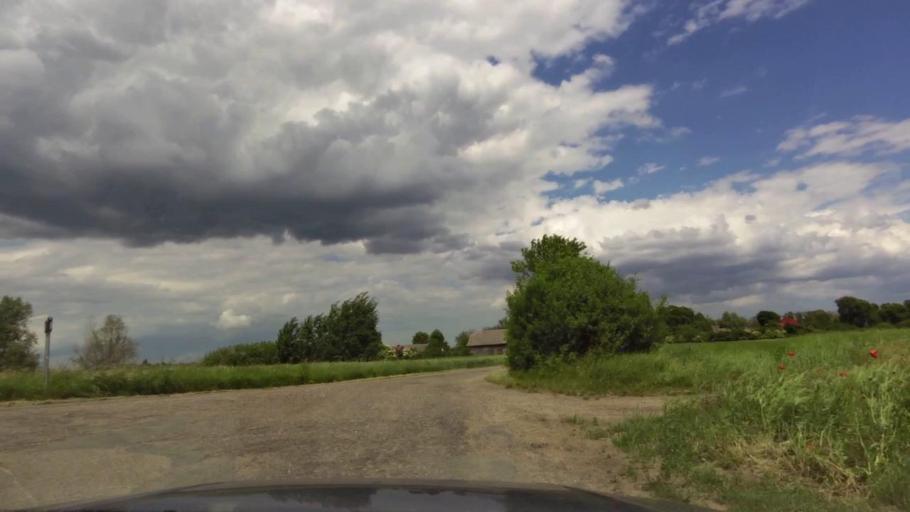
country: PL
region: West Pomeranian Voivodeship
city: Trzcinsko Zdroj
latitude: 52.9434
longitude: 14.7172
